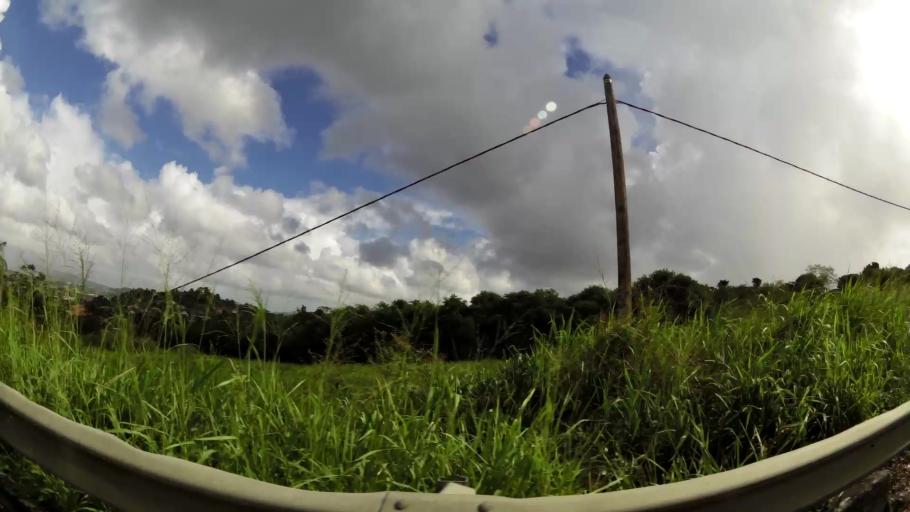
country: MQ
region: Martinique
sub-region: Martinique
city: Les Trois-Ilets
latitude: 14.5156
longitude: -60.9835
